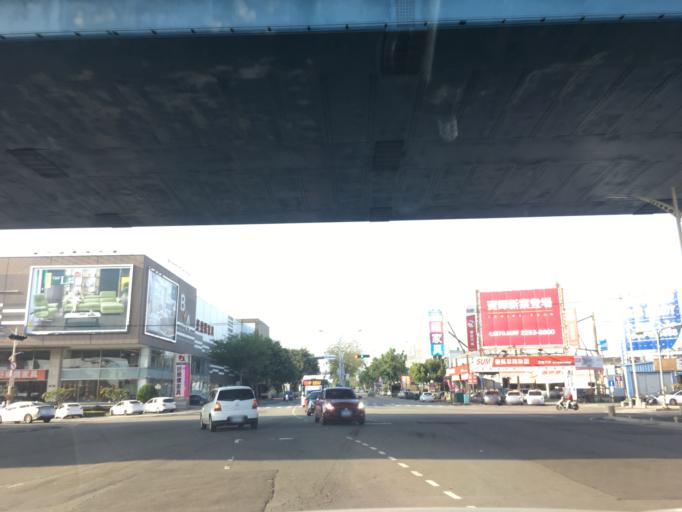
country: TW
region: Taiwan
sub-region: Taichung City
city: Taichung
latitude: 24.2008
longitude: 120.6867
